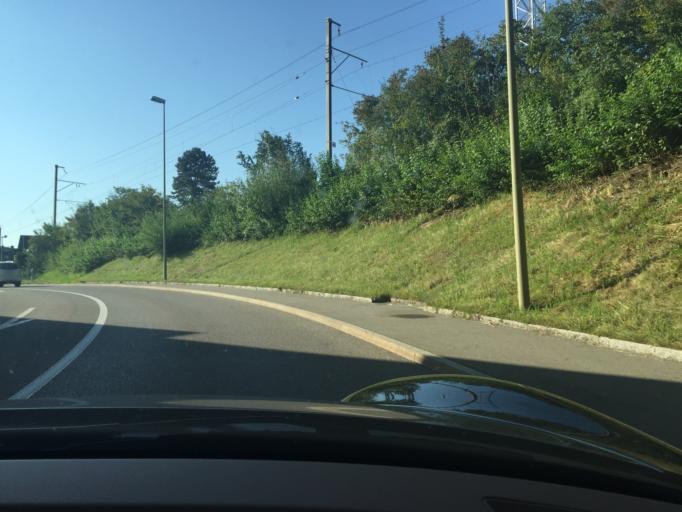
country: CH
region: Zurich
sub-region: Bezirk Uster
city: Aesch
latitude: 47.3240
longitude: 8.6580
